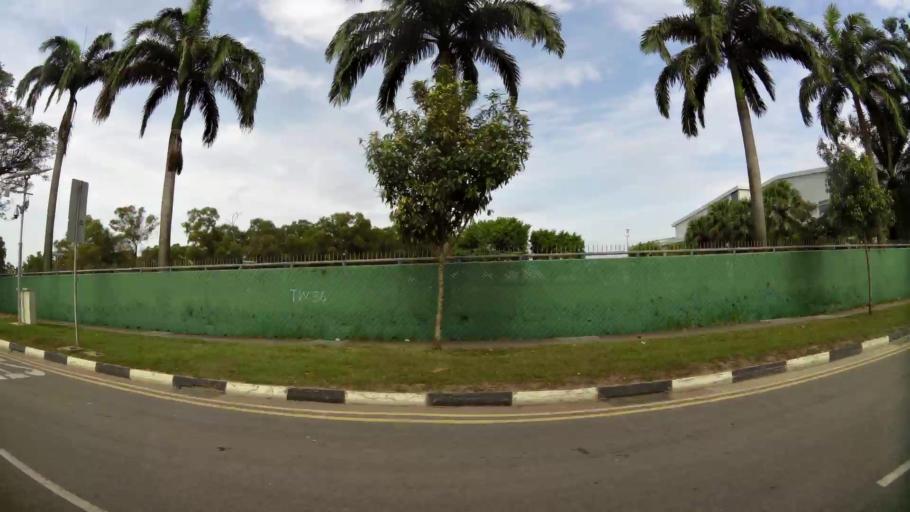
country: MY
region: Johor
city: Johor Bahru
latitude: 1.3260
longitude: 103.6314
